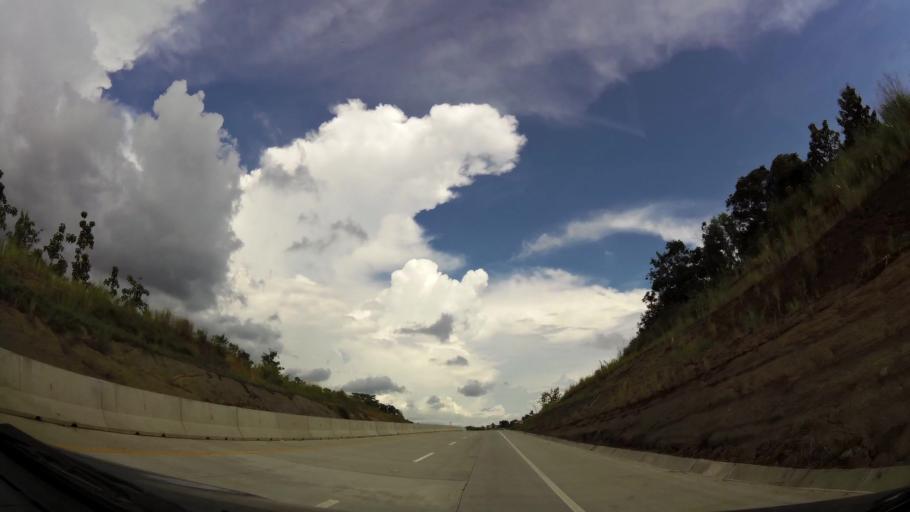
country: PA
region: Panama
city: San Miguelito
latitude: 9.0901
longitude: -79.4392
